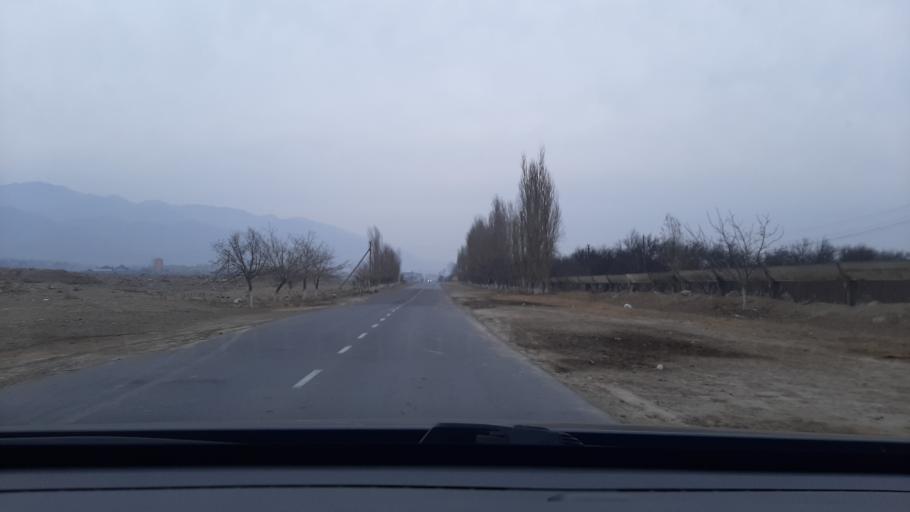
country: TJ
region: Viloyati Sughd
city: Khujand
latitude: 40.2705
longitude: 69.5741
